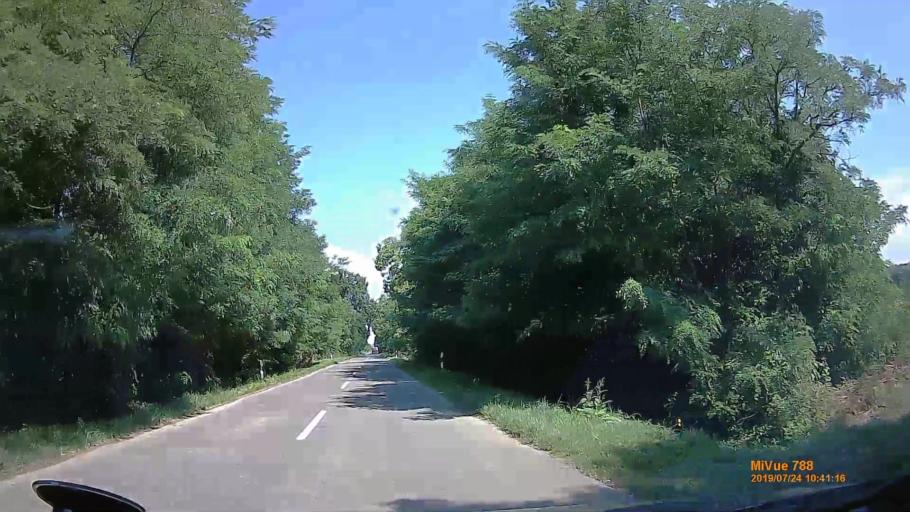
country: HU
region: Szabolcs-Szatmar-Bereg
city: Tarpa
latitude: 48.1855
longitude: 22.5488
